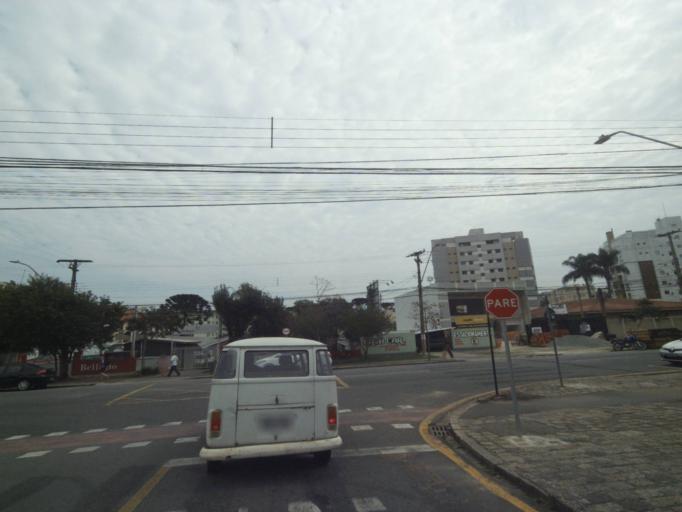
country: BR
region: Parana
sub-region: Curitiba
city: Curitiba
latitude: -25.4515
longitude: -49.3023
